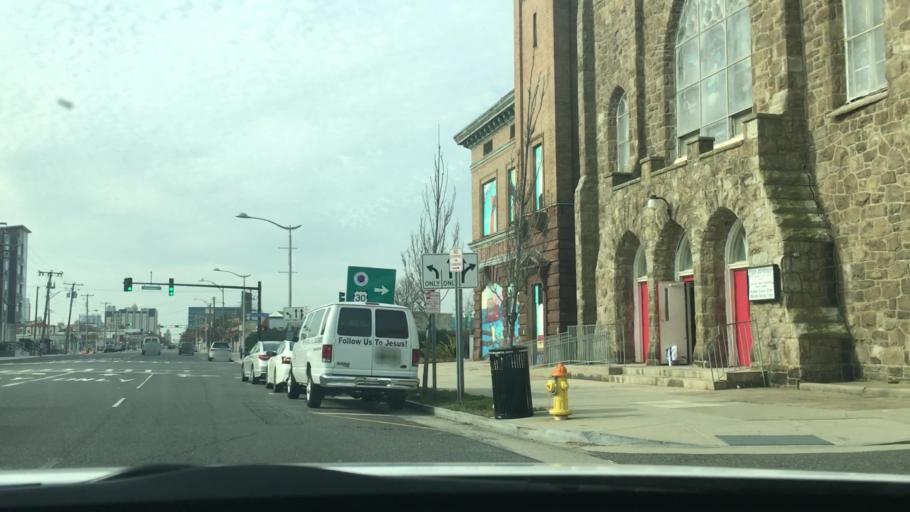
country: US
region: New Jersey
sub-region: Atlantic County
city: Atlantic City
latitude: 39.3666
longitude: -74.4174
